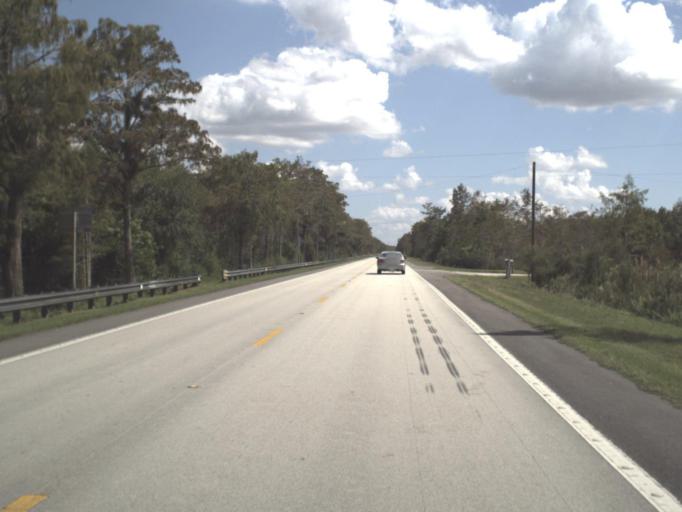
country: US
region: Florida
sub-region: Miami-Dade County
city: Kendall West
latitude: 25.8181
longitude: -80.8880
